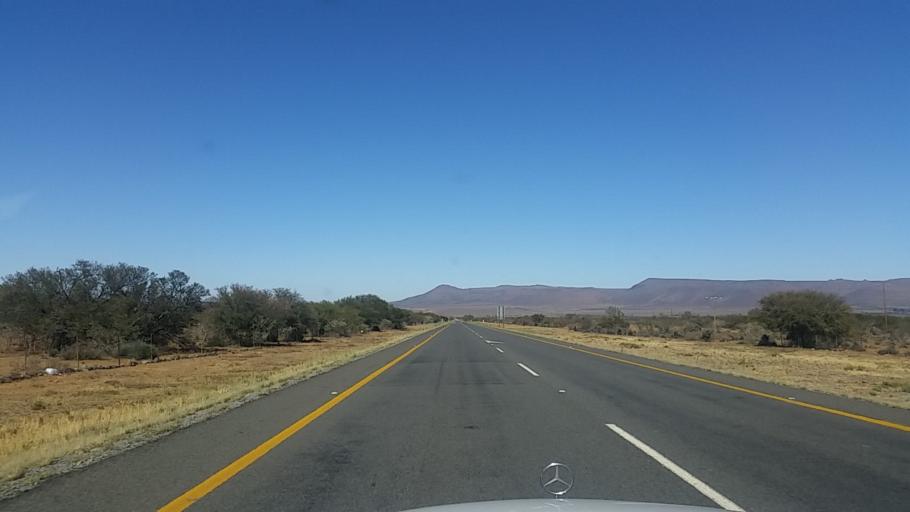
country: ZA
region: Eastern Cape
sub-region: Cacadu District Municipality
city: Graaff-Reinet
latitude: -31.9812
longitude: 24.6995
